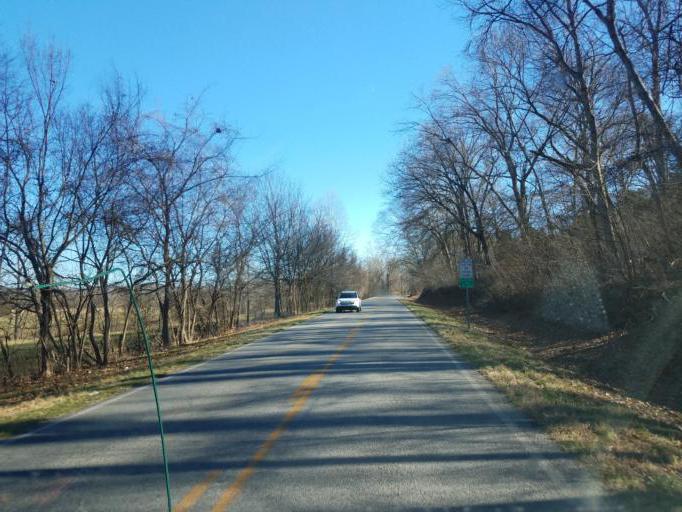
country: US
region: Arkansas
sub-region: Washington County
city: Elkins
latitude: 36.0330
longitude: -93.9449
